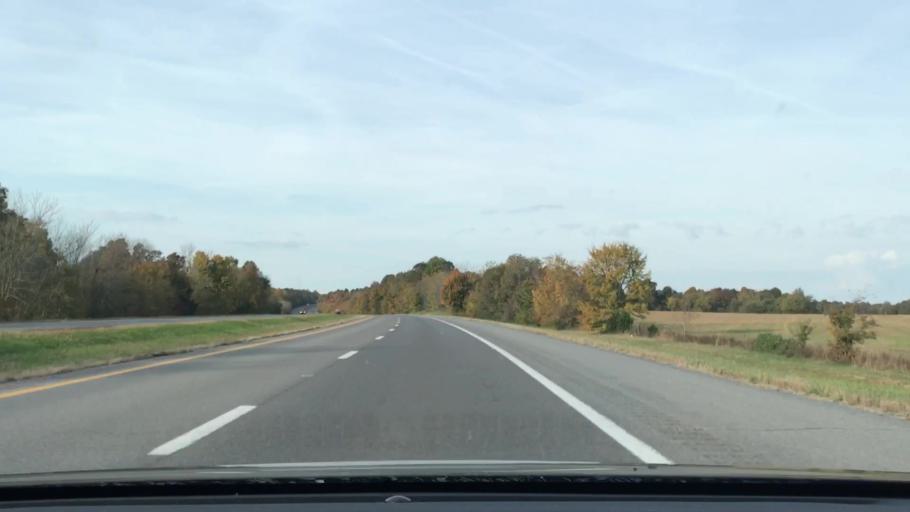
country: US
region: Kentucky
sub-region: Marshall County
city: Benton
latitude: 36.8461
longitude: -88.4064
